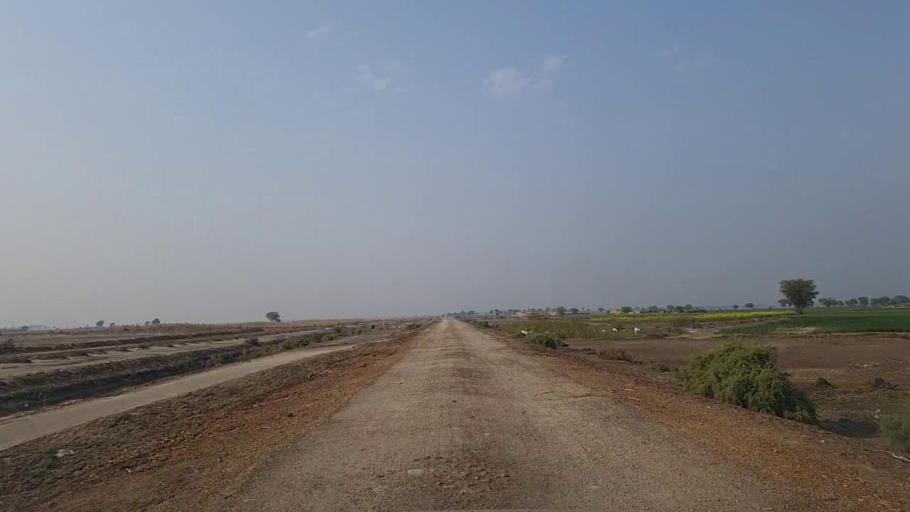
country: PK
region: Sindh
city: Nawabshah
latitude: 26.3304
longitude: 68.4764
